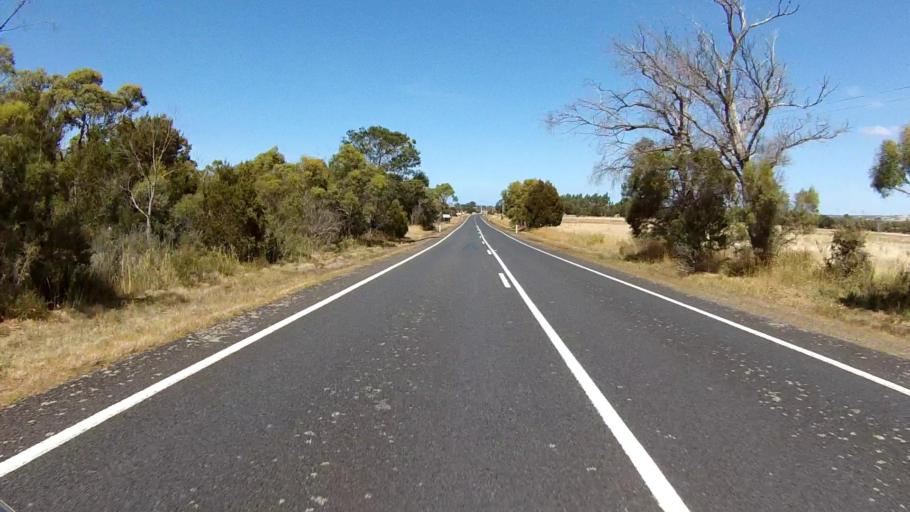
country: AU
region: Tasmania
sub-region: Break O'Day
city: St Helens
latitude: -42.0560
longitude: 148.0585
